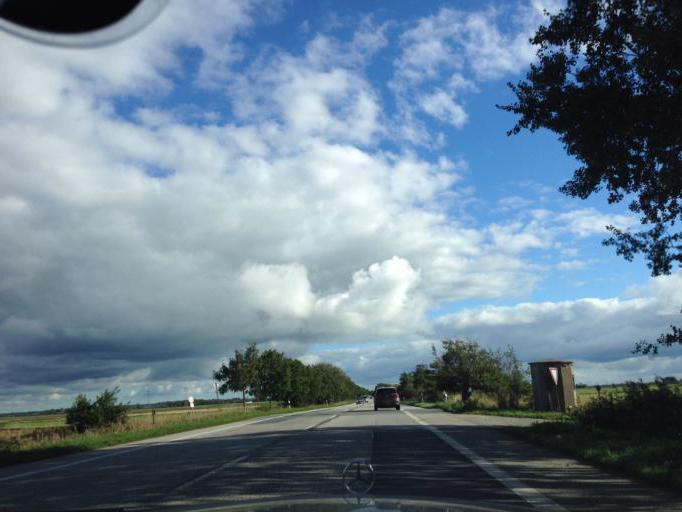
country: DE
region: Schleswig-Holstein
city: Risum-Lindholm
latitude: 54.7572
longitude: 8.8866
